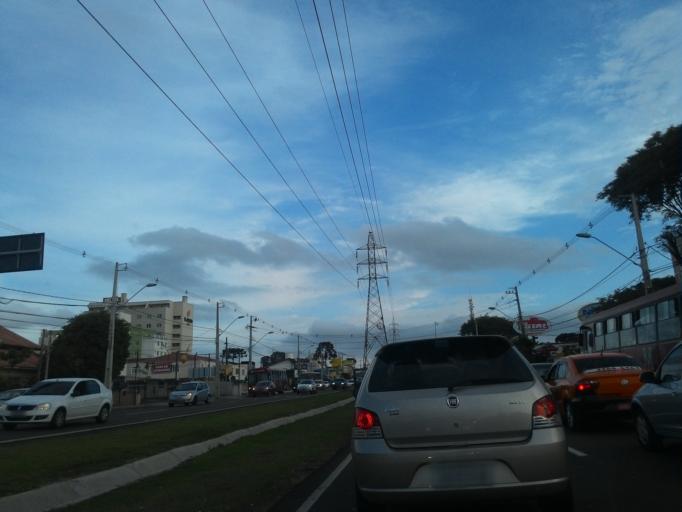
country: BR
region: Parana
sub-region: Curitiba
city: Curitiba
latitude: -25.4567
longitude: -49.2406
